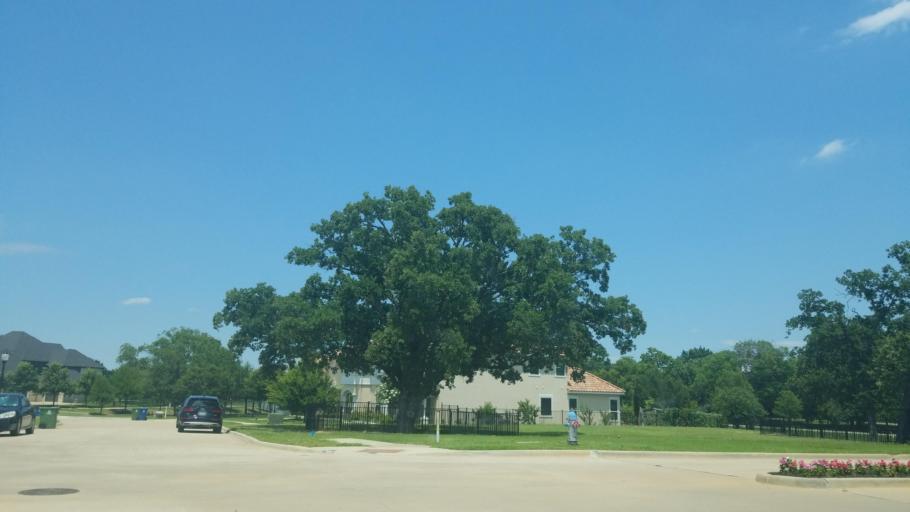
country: US
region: Texas
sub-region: Denton County
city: Copper Canyon
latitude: 33.0769
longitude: -97.0877
